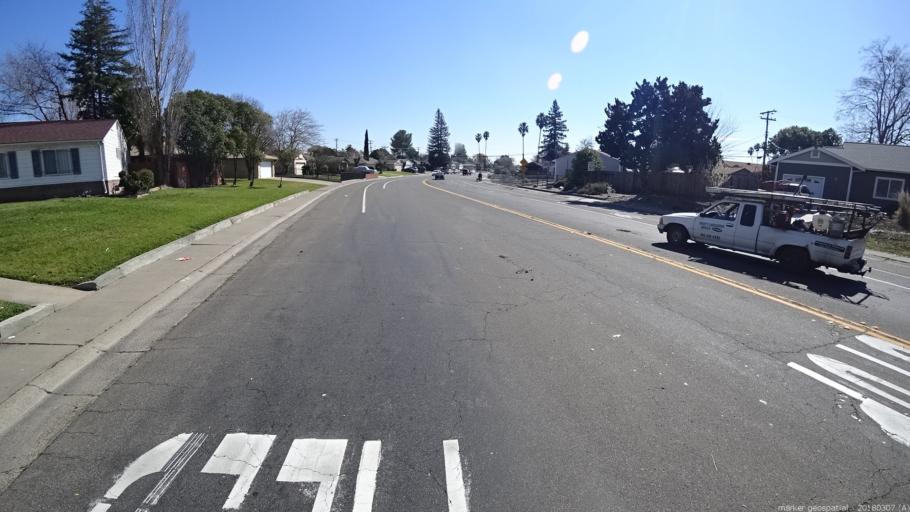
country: US
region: California
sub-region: Sacramento County
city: Parkway
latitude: 38.4998
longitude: -121.4424
